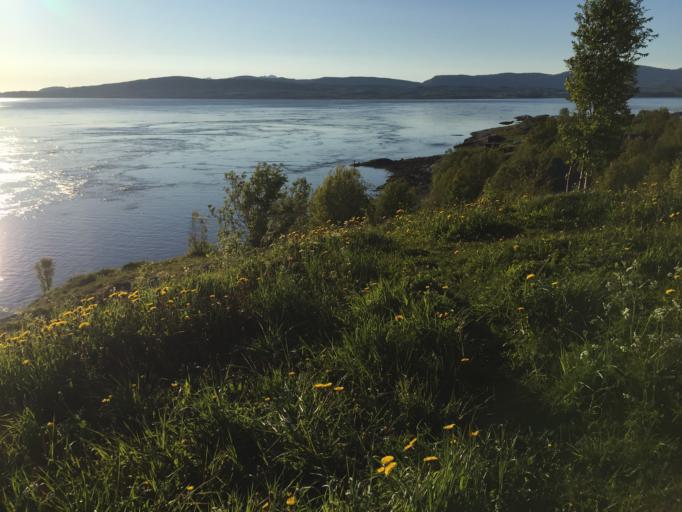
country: NO
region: Nordland
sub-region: Bodo
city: Loding
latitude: 67.2356
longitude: 14.6148
